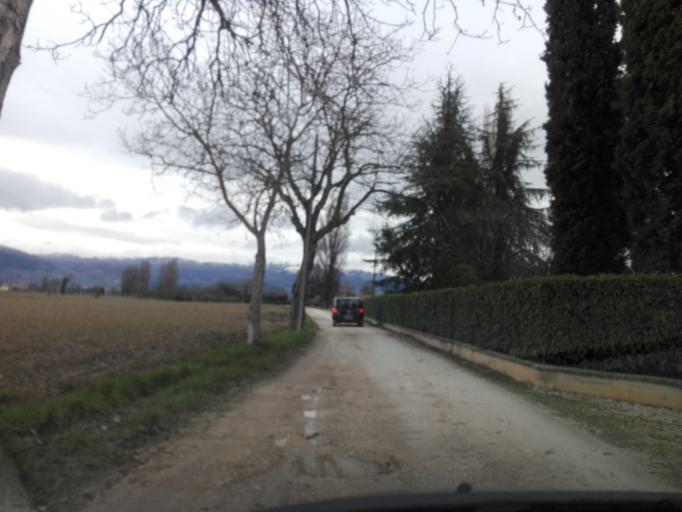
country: IT
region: Umbria
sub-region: Provincia di Perugia
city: Bevagna
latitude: 42.9471
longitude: 12.6467
